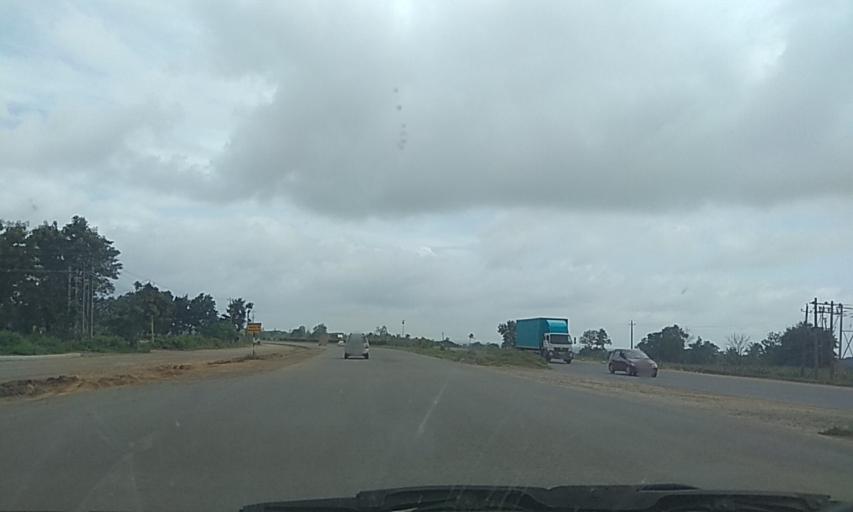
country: IN
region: Karnataka
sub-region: Dharwad
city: Kundgol
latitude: 15.1760
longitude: 75.1398
